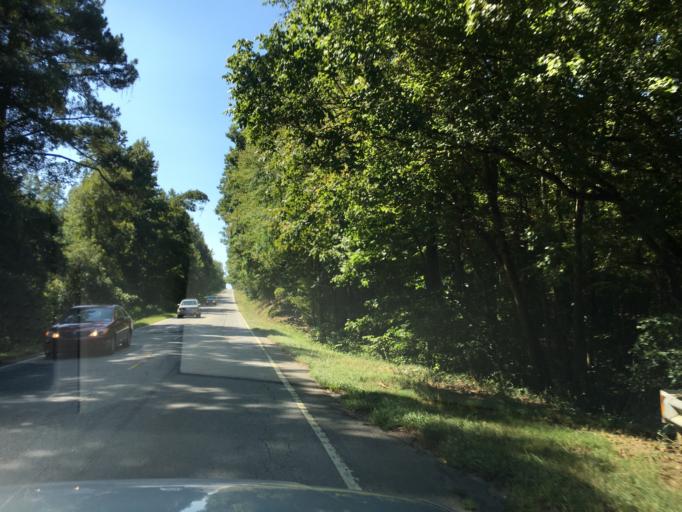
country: US
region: South Carolina
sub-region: Laurens County
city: Joanna
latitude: 34.2851
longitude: -81.8469
